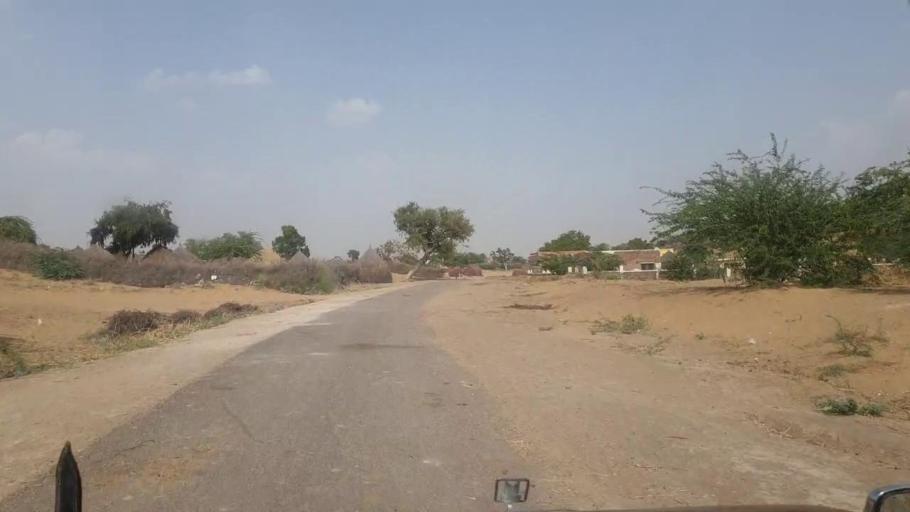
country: PK
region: Sindh
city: Islamkot
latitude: 25.2341
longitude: 70.2860
